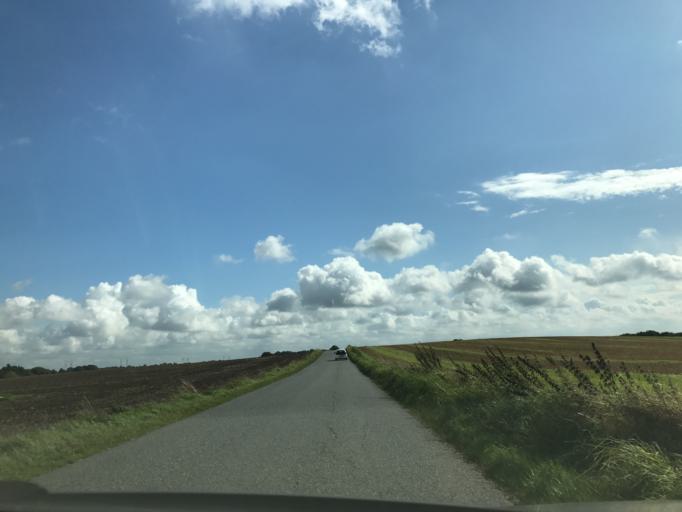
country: DK
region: South Denmark
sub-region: Middelfart Kommune
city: Norre Aby
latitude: 55.4490
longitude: 9.8159
